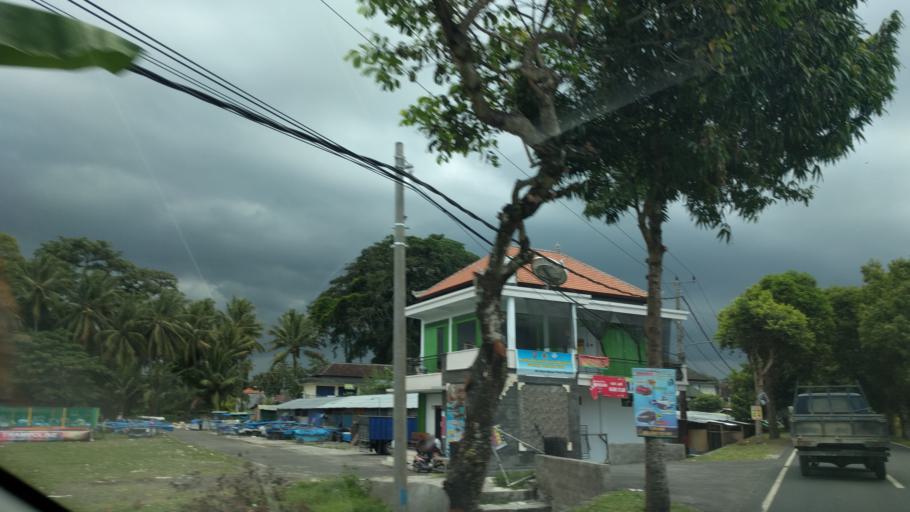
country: ID
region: Bali
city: Banjar Pande
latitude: -8.5207
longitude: 115.2408
